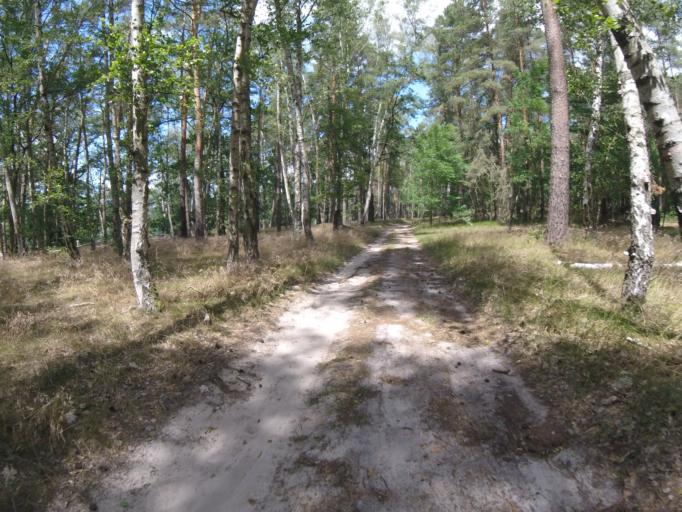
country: DE
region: Brandenburg
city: Gross Koris
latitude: 52.2044
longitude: 13.6397
